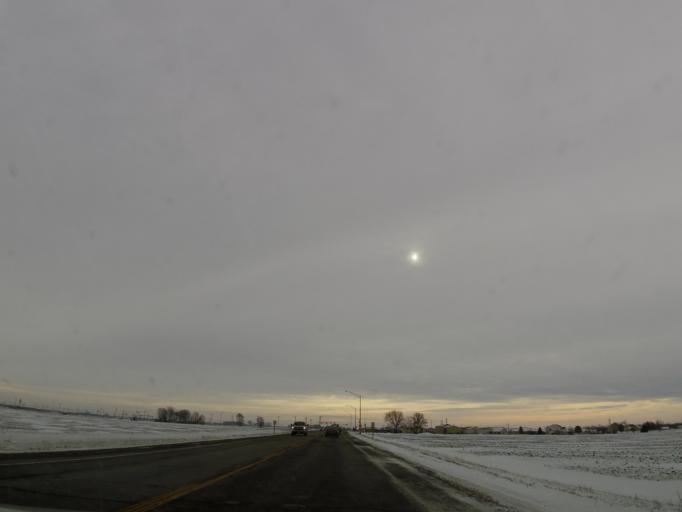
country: US
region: Illinois
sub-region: LaSalle County
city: La Salle
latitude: 41.2983
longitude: -89.1041
